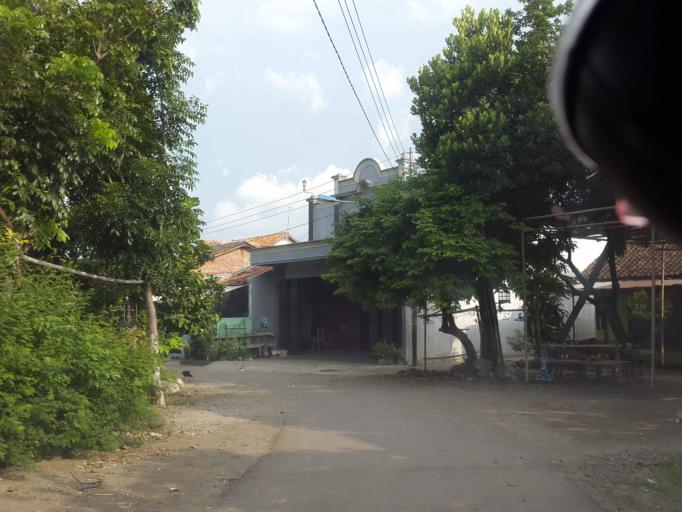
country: ID
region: Central Java
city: Tegal
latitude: -6.8740
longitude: 109.1469
